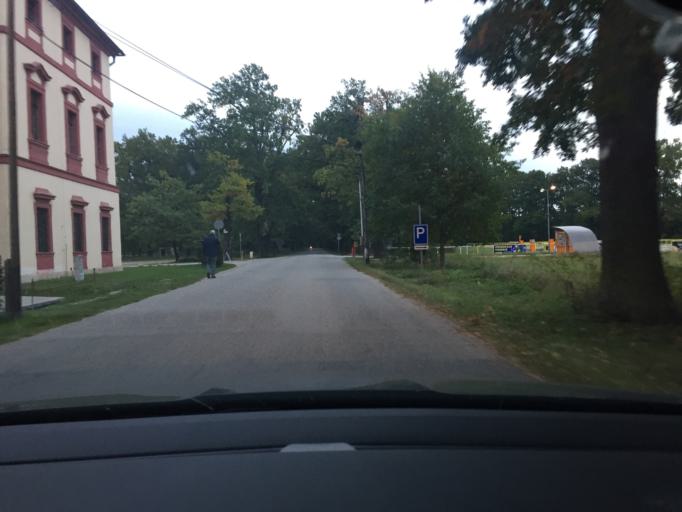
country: CZ
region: Jihocesky
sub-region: Okres Ceske Budejovice
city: Hluboka nad Vltavou
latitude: 49.0412
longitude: 14.4216
